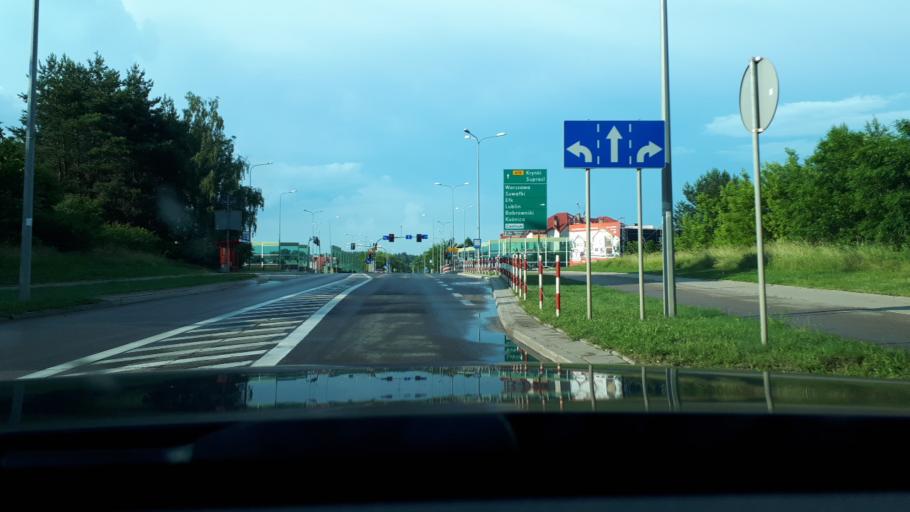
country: PL
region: Podlasie
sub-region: Powiat bialostocki
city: Wasilkow
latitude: 53.1594
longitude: 23.1980
